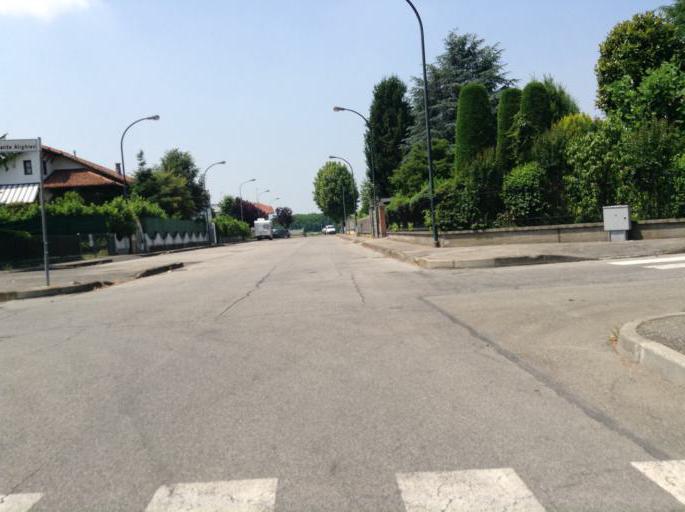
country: IT
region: Piedmont
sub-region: Provincia di Torino
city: Carignano
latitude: 44.9135
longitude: 7.6754
